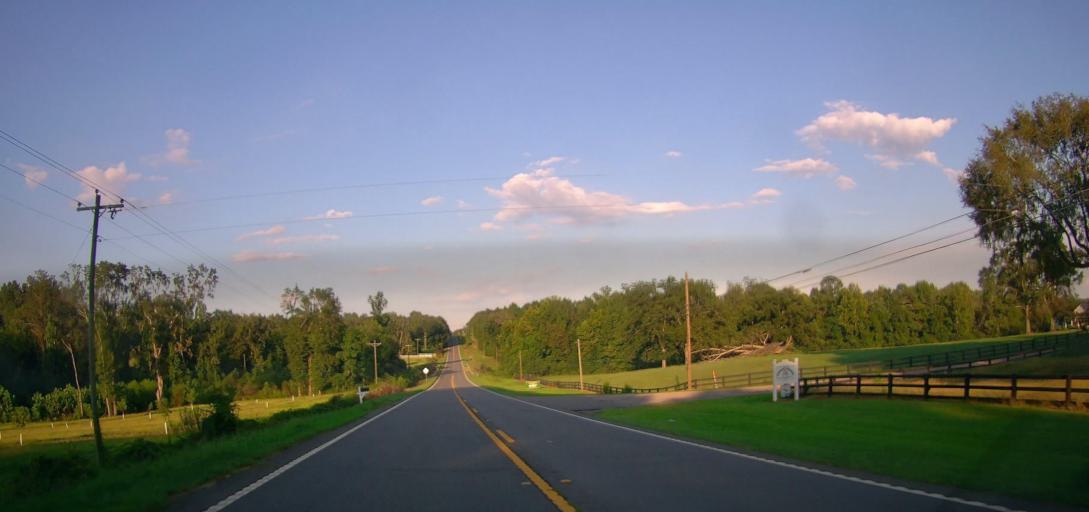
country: US
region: Georgia
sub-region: Crawford County
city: Roberta
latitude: 32.6990
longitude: -84.0477
